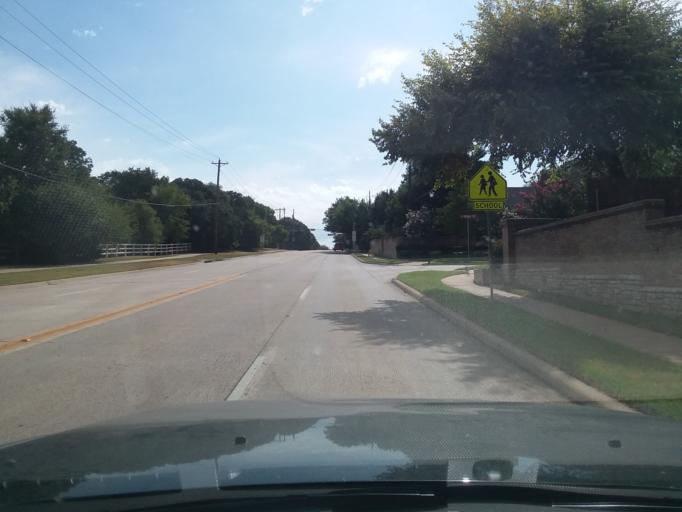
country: US
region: Texas
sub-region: Denton County
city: Flower Mound
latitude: 33.0138
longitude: -97.0813
